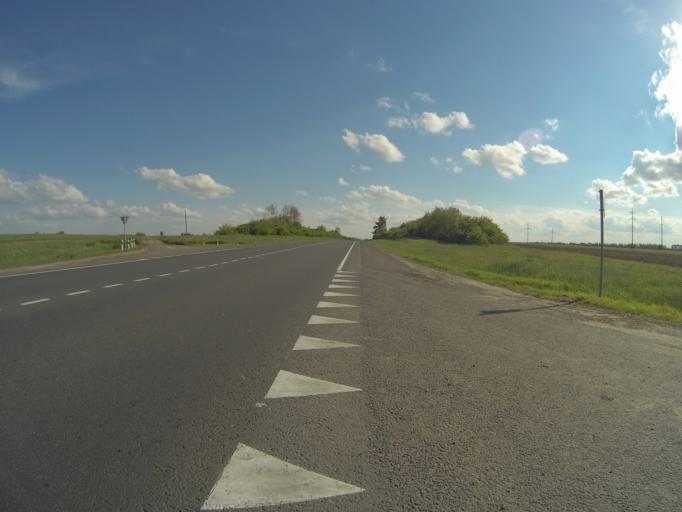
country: RU
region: Vladimir
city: Suzdal'
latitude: 56.3973
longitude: 40.4661
